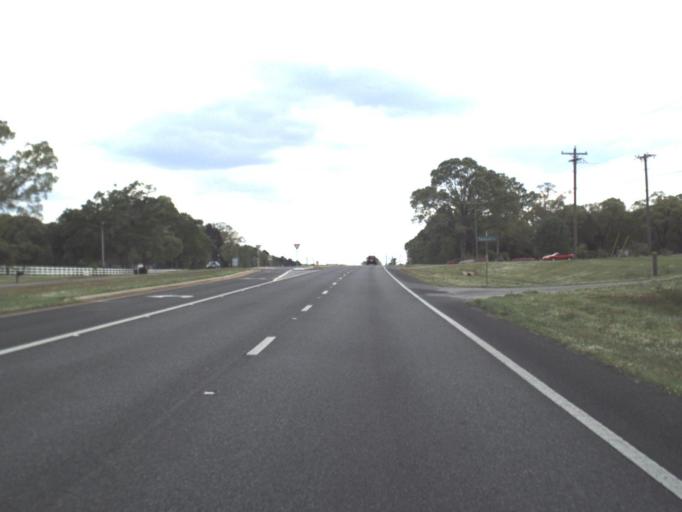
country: US
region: Florida
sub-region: Okaloosa County
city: Crestview
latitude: 30.8003
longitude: -86.5558
